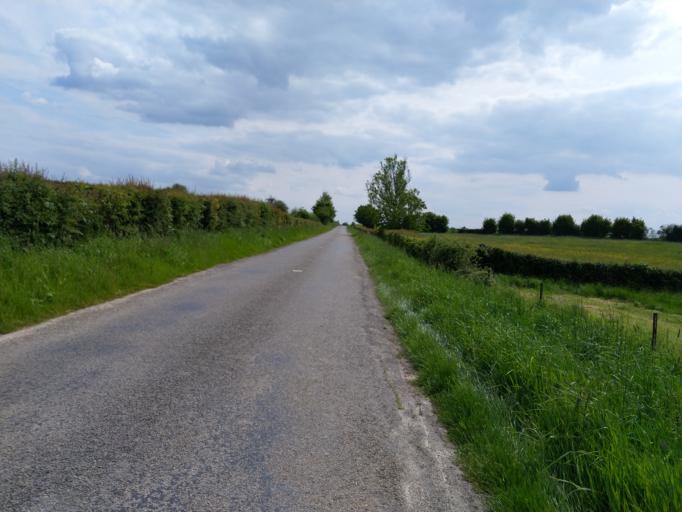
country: FR
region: Picardie
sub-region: Departement de l'Aisne
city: Boue
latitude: 50.0314
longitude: 3.6798
